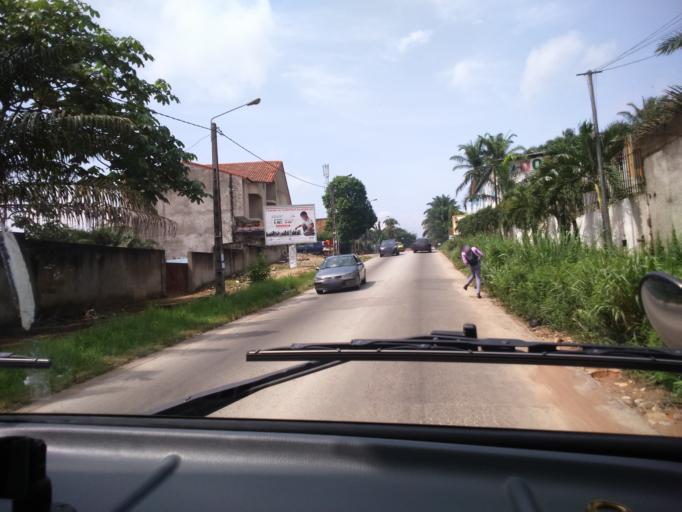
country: CI
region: Lagunes
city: Abidjan
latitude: 5.3597
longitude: -3.9785
